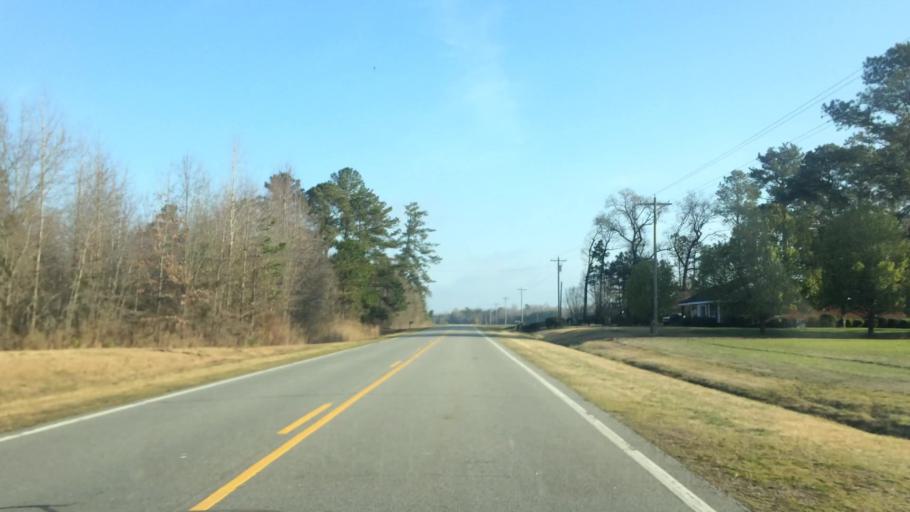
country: US
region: North Carolina
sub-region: Edgecombe County
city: Pinetops
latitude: 35.7068
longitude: -77.6332
